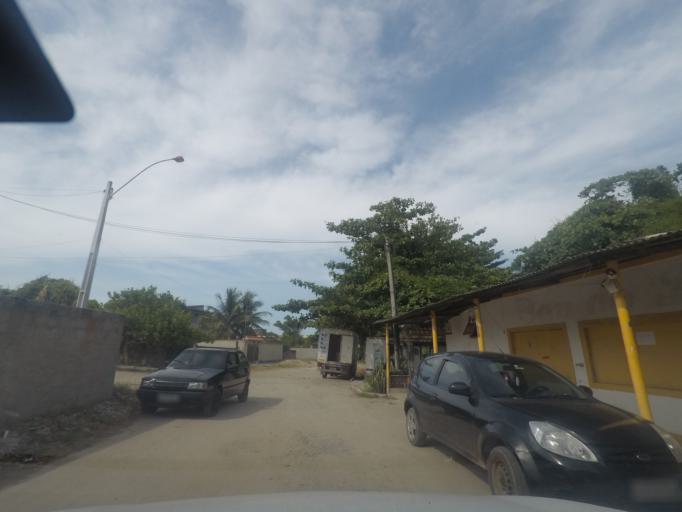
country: BR
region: Rio de Janeiro
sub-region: Marica
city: Marica
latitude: -22.9544
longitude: -42.8120
